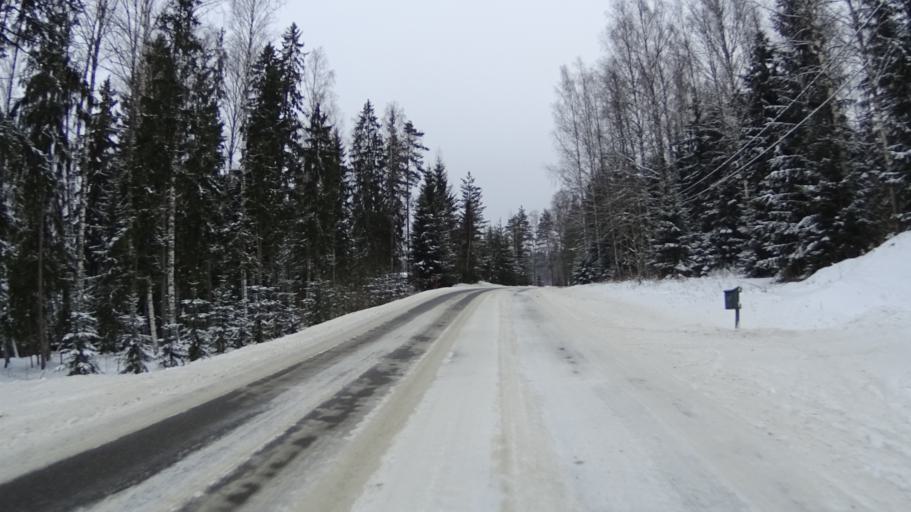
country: FI
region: Uusimaa
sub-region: Helsinki
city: Karkkila
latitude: 60.5032
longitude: 24.1399
